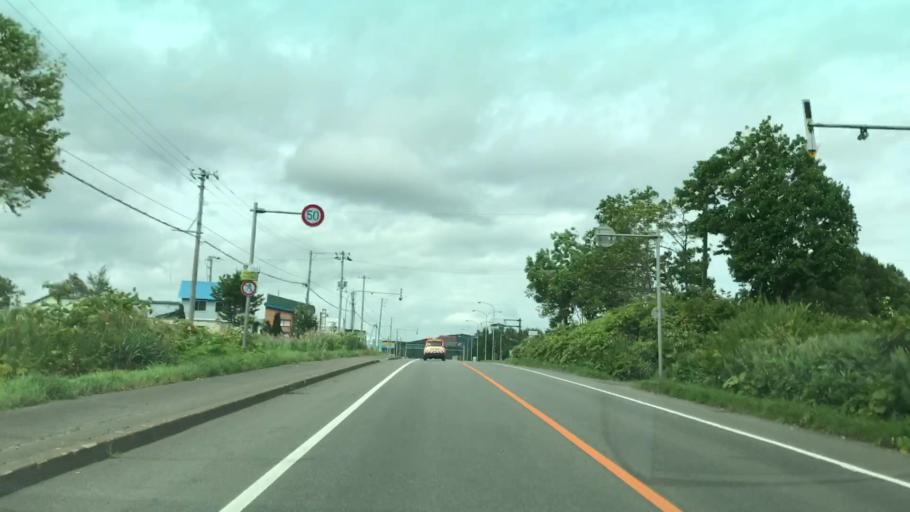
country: JP
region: Hokkaido
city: Niseko Town
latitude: 42.9137
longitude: 140.7513
